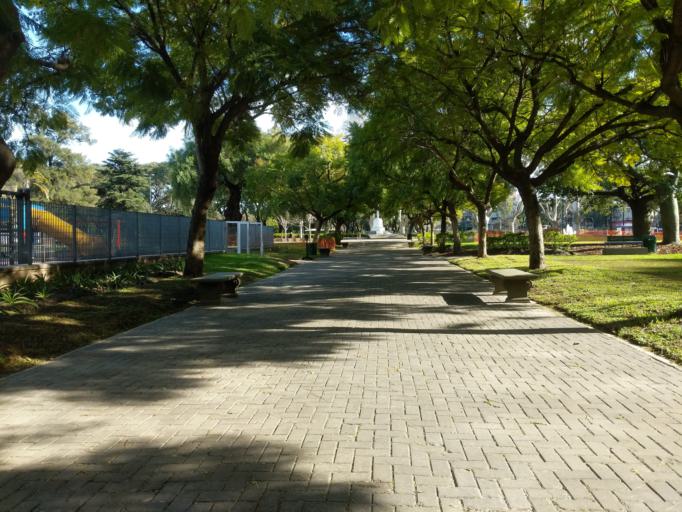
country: AR
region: Buenos Aires F.D.
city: Colegiales
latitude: -34.5903
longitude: -58.4501
